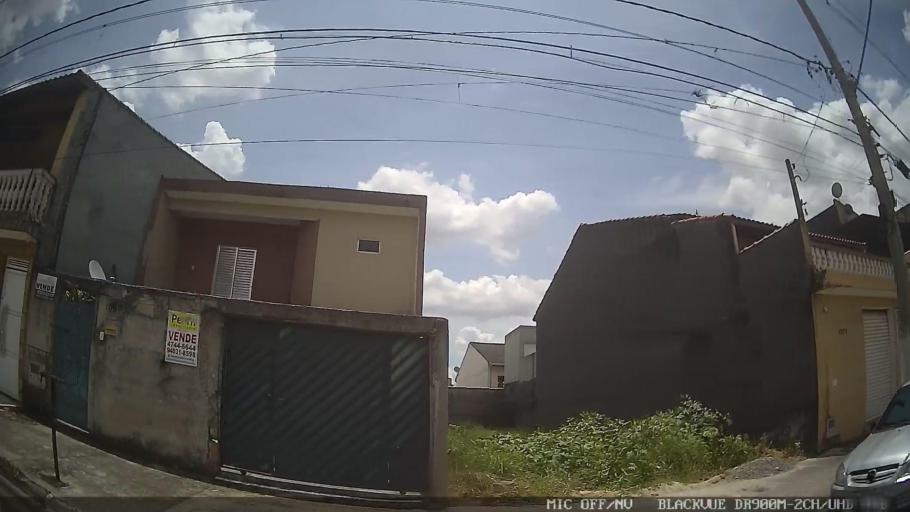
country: BR
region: Sao Paulo
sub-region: Suzano
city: Suzano
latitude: -23.5440
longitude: -46.3245
